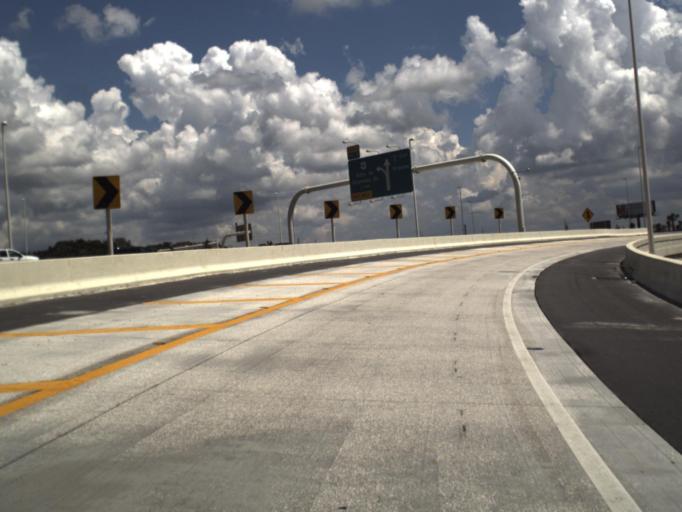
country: US
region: Florida
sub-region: Hillsborough County
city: Tampa
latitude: 27.9639
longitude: -82.4253
